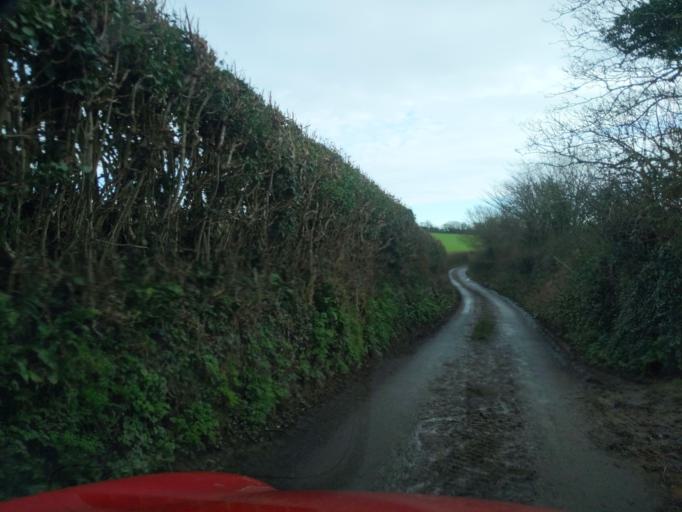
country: GB
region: England
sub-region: Devon
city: Salcombe
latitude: 50.2635
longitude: -3.6870
